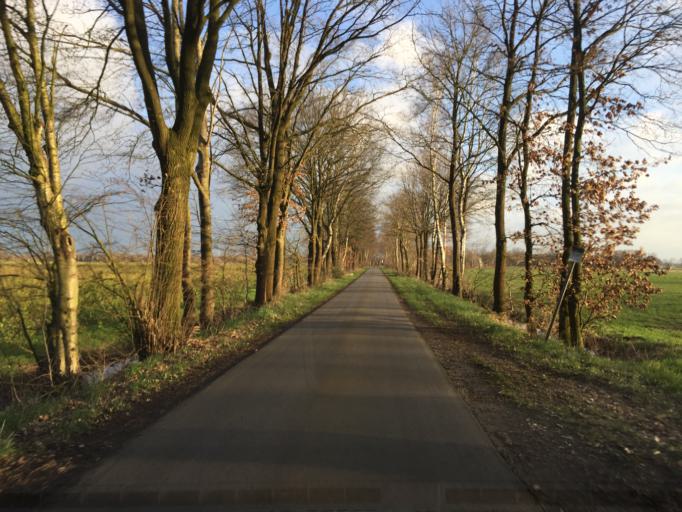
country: DE
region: Lower Saxony
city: Borstel
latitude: 52.6134
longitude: 8.9184
